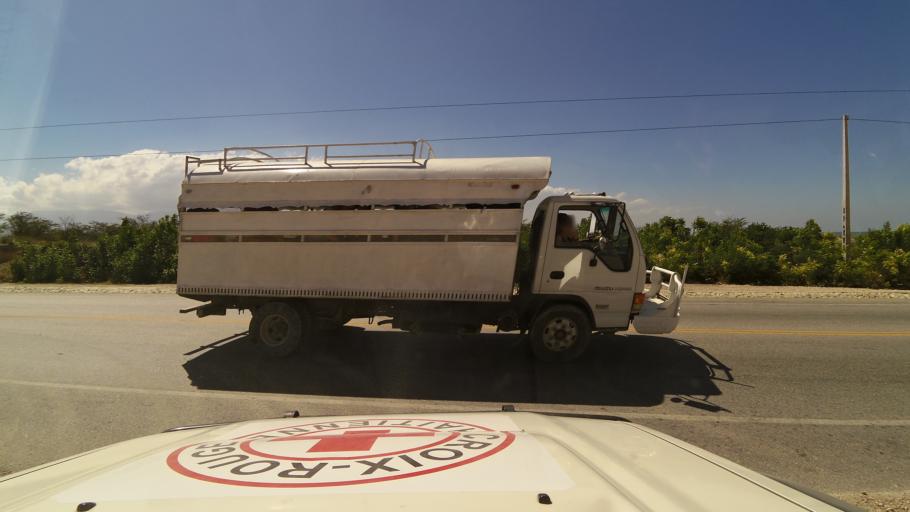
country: HT
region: Ouest
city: Croix des Bouquets
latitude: 18.6668
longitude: -72.2981
